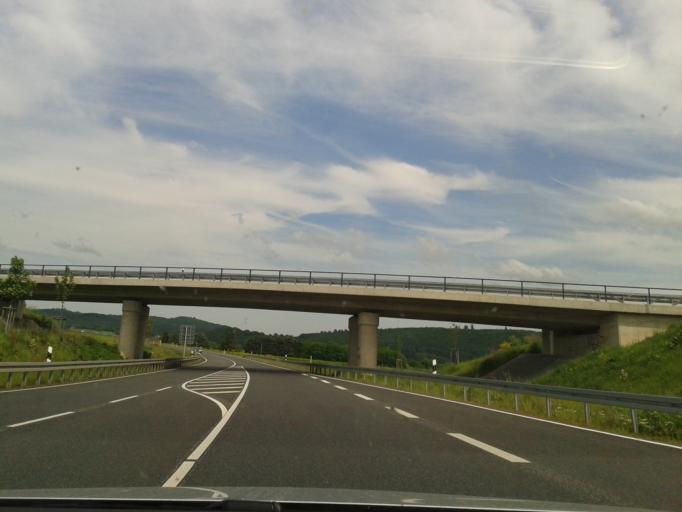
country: DE
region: Hesse
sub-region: Regierungsbezirk Giessen
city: Fronhausen
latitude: 50.7525
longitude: 8.7217
